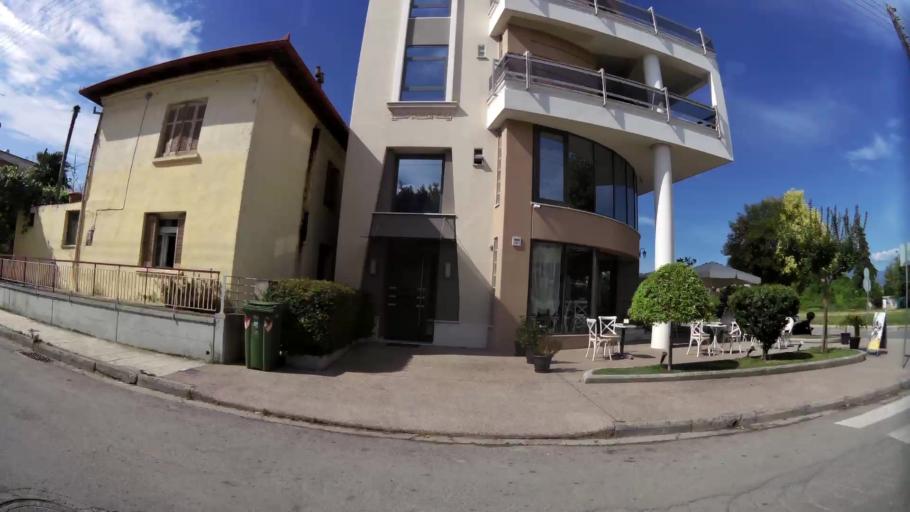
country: GR
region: Central Macedonia
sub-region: Nomos Pierias
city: Katerini
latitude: 40.2775
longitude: 22.5119
